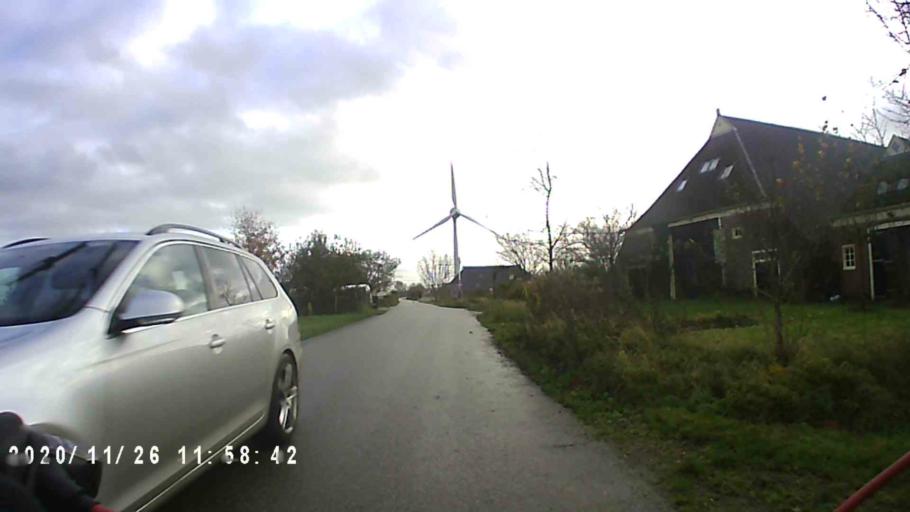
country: NL
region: Groningen
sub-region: Gemeente Bedum
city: Bedum
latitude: 53.3142
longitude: 6.6043
